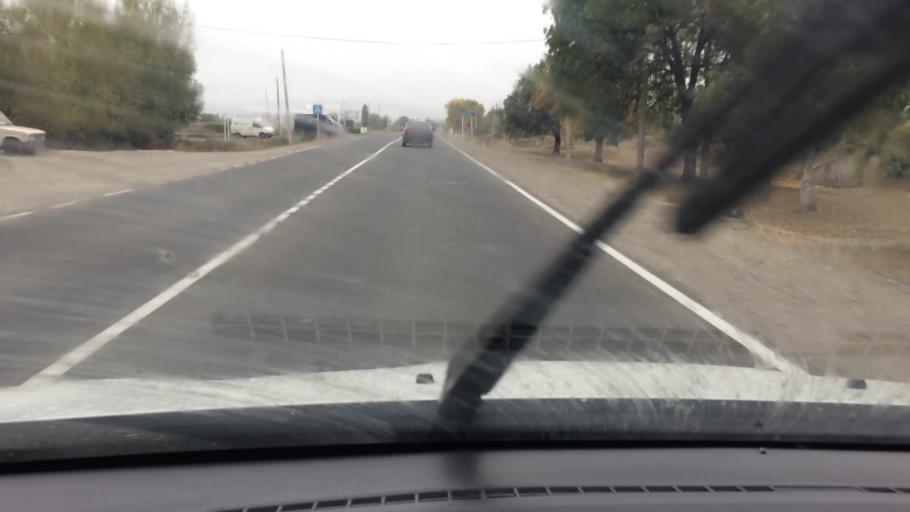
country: GE
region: Kvemo Kartli
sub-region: Marneuli
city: Marneuli
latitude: 41.4213
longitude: 44.8247
